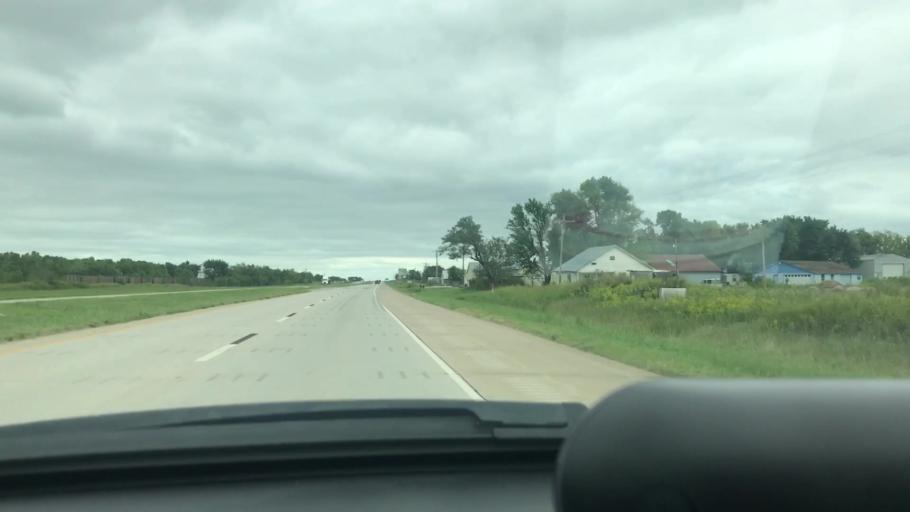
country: US
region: Oklahoma
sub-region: Mayes County
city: Chouteau
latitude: 36.0985
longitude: -95.3627
